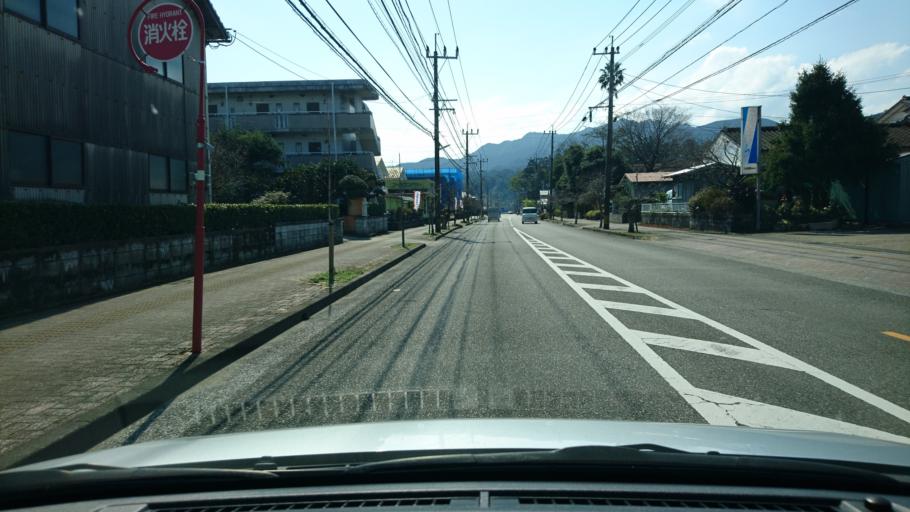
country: JP
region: Miyazaki
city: Miyazaki-shi
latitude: 31.8294
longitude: 131.4201
